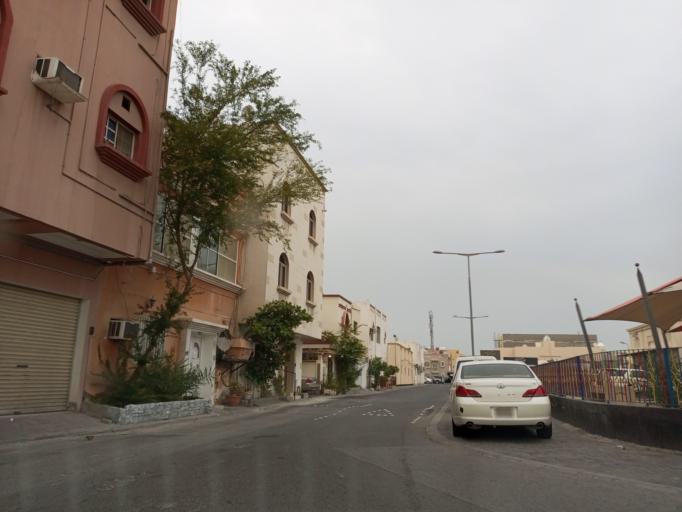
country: BH
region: Muharraq
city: Al Muharraq
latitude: 26.2576
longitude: 50.6330
